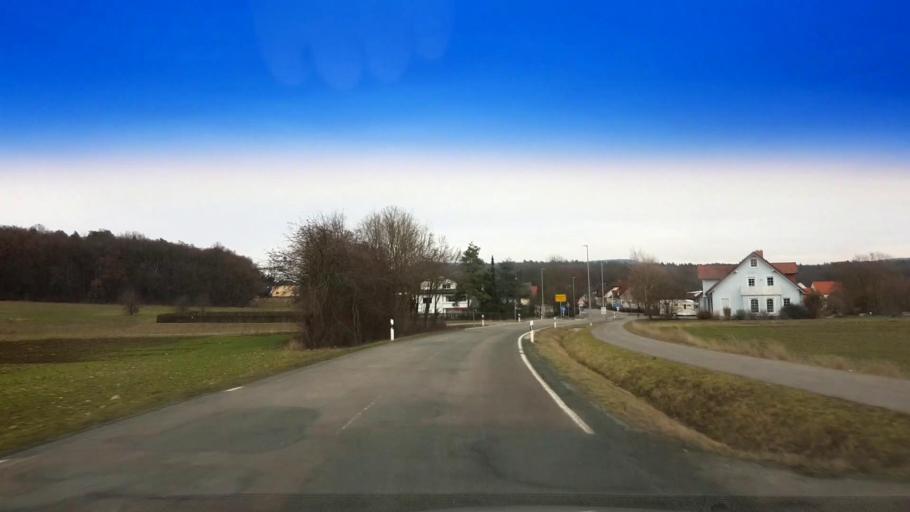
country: DE
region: Bavaria
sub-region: Upper Franconia
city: Memmelsdorf
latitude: 49.9327
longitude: 10.9748
